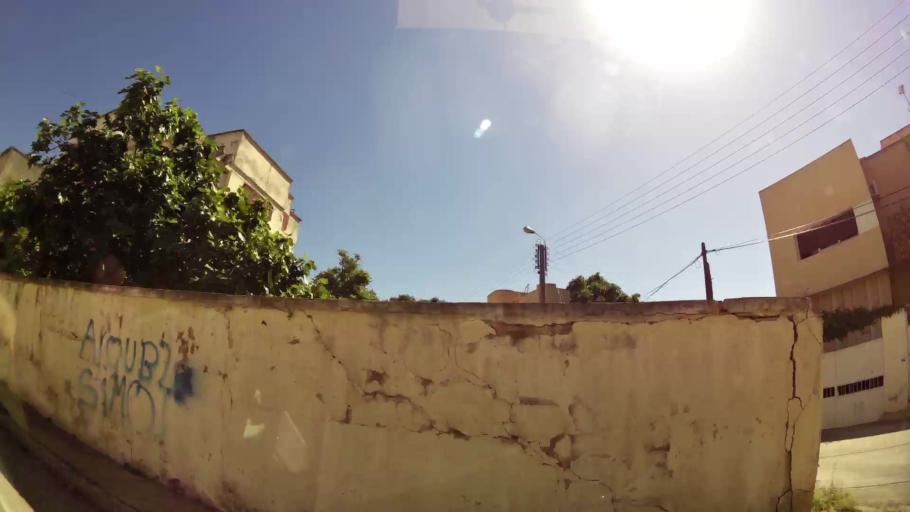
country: MA
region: Fes-Boulemane
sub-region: Fes
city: Fes
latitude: 34.0244
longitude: -4.9920
